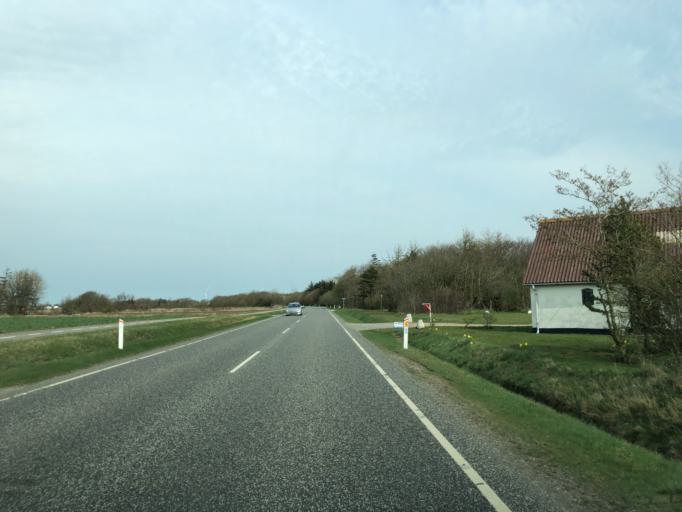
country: DK
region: Central Jutland
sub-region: Ringkobing-Skjern Kommune
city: Skjern
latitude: 55.8440
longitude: 8.3594
